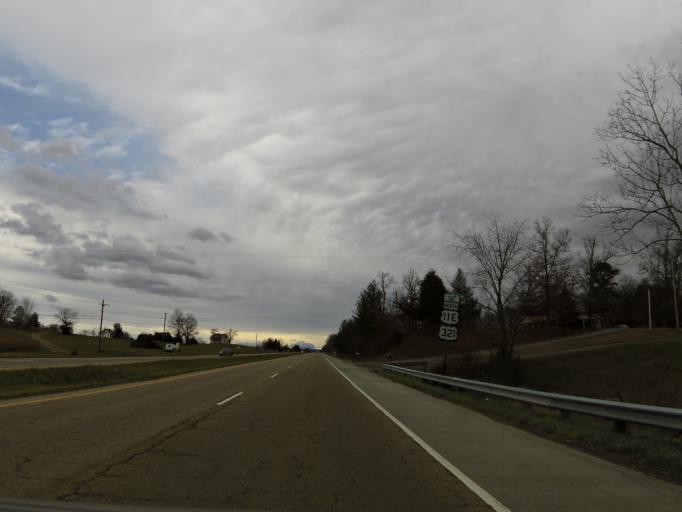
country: US
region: Tennessee
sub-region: Greene County
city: Tusculum
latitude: 36.2379
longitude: -82.6265
